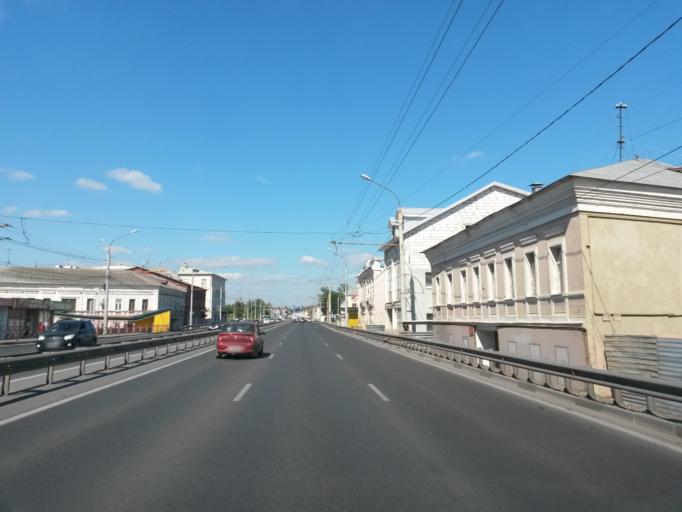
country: RU
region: Jaroslavl
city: Yaroslavl
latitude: 57.6098
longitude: 39.8814
